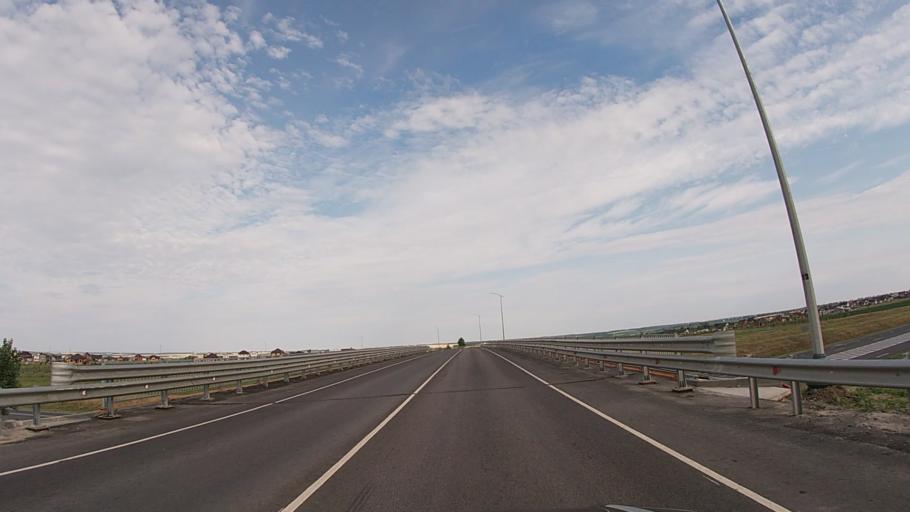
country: RU
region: Belgorod
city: Severnyy
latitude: 50.6747
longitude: 36.4736
